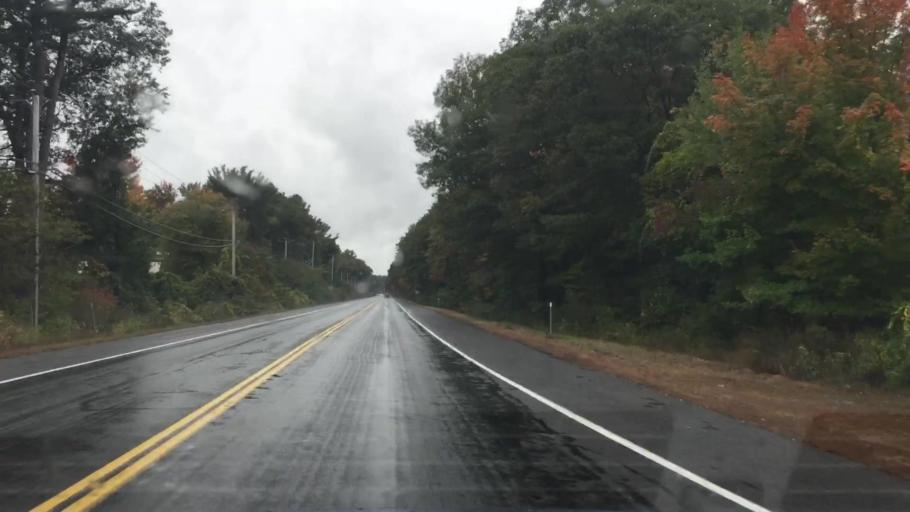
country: US
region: Massachusetts
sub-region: Essex County
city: Salisbury
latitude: 42.8700
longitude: -70.8450
